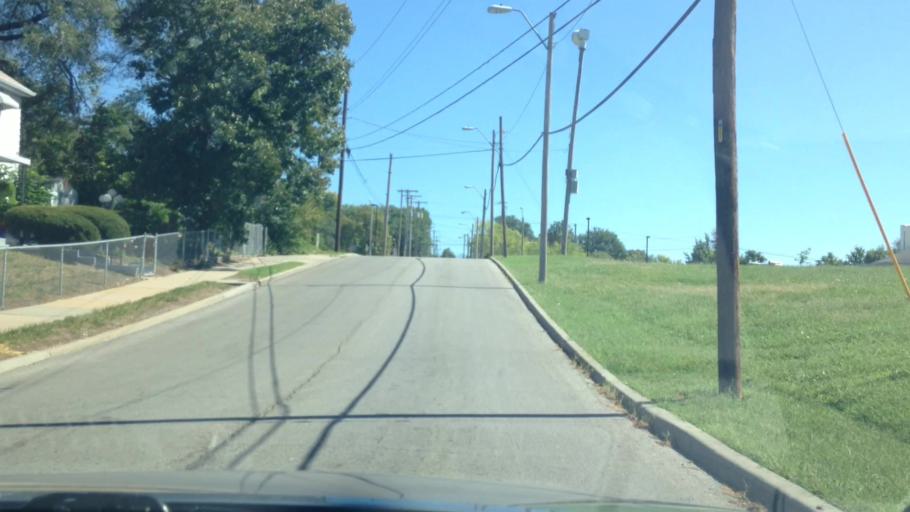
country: US
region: Missouri
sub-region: Jackson County
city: Kansas City
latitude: 39.0484
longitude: -94.5563
